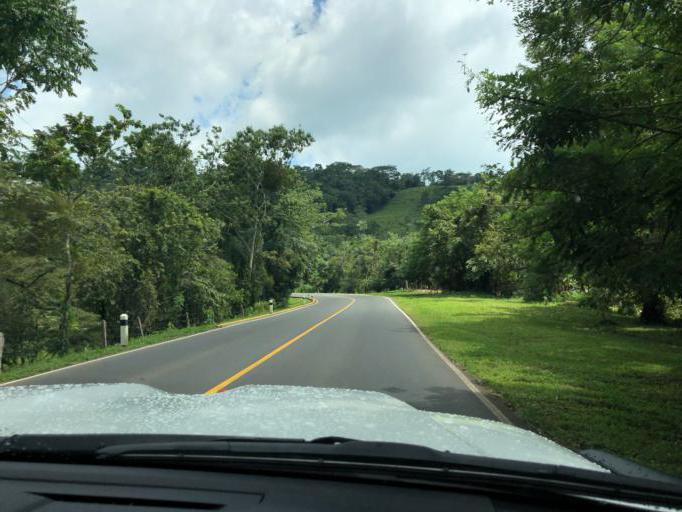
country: NI
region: Chontales
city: Villa Sandino
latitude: 11.9947
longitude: -84.9047
